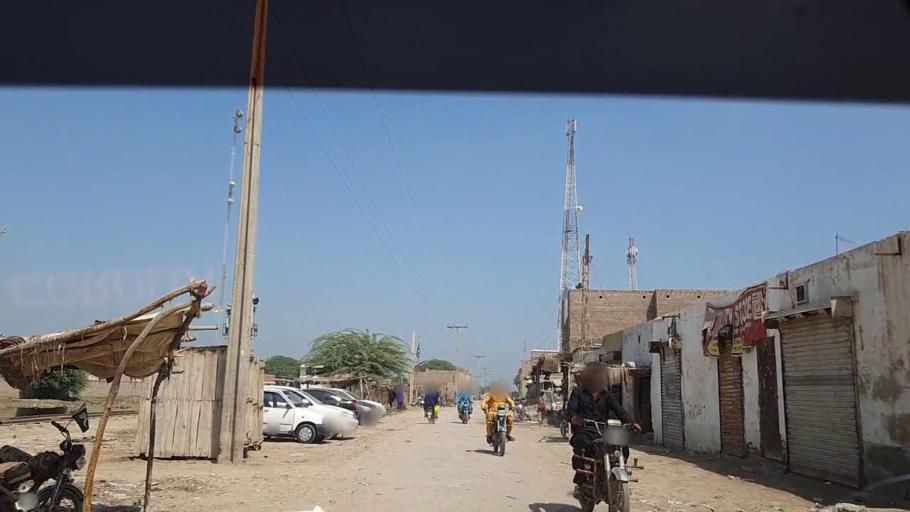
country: PK
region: Sindh
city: Tangwani
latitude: 28.2779
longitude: 68.9985
